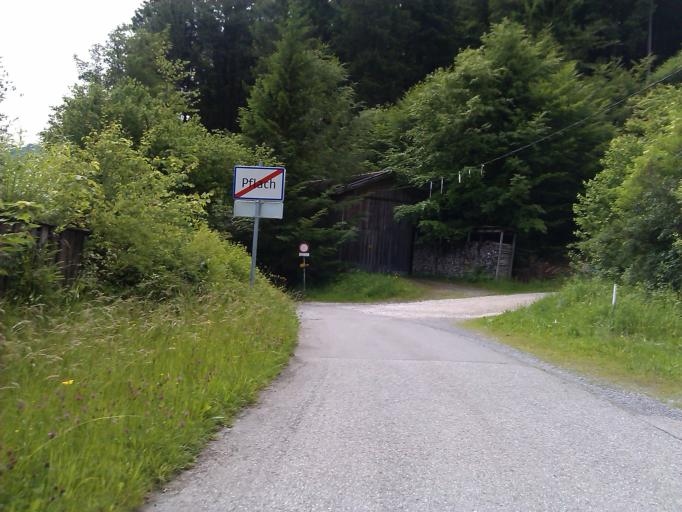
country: AT
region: Tyrol
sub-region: Politischer Bezirk Reutte
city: Pflach
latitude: 47.5106
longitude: 10.7073
